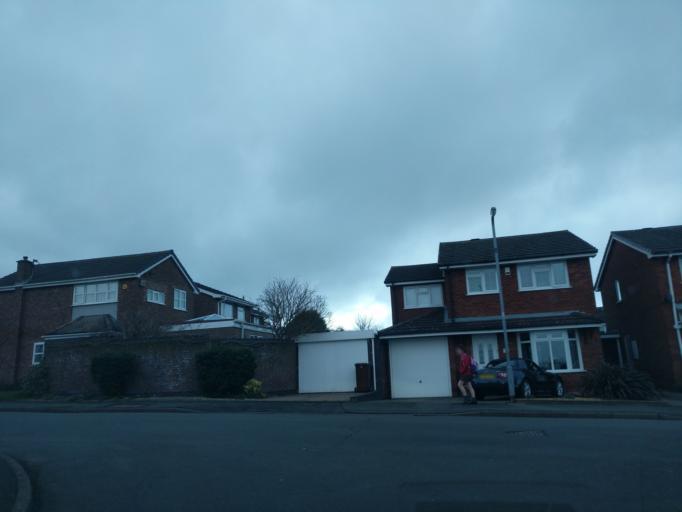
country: GB
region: England
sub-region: Staffordshire
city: Cannock
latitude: 52.7157
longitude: -2.0173
